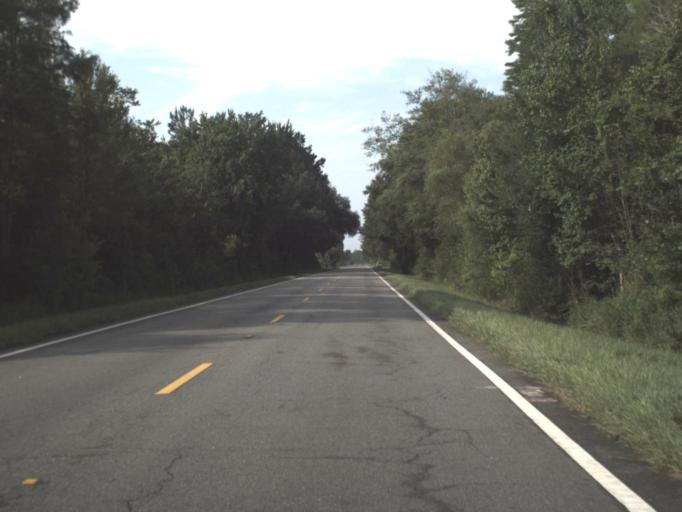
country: US
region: Florida
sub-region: Madison County
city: Madison
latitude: 30.3815
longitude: -83.6577
